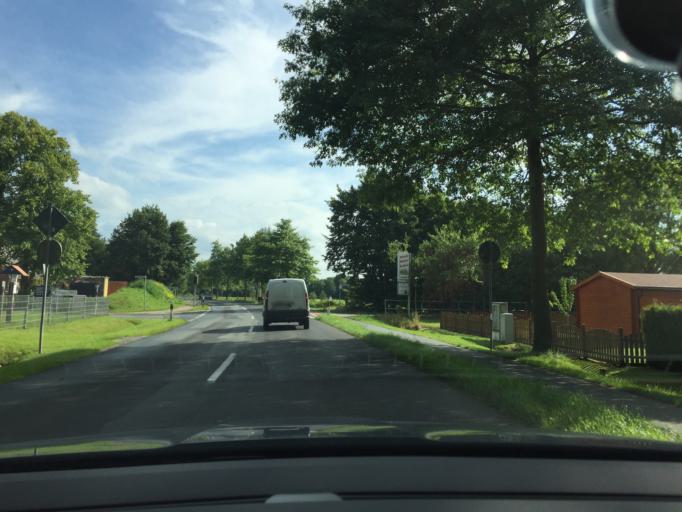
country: DE
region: Lower Saxony
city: Aurich
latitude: 53.4443
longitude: 7.4766
